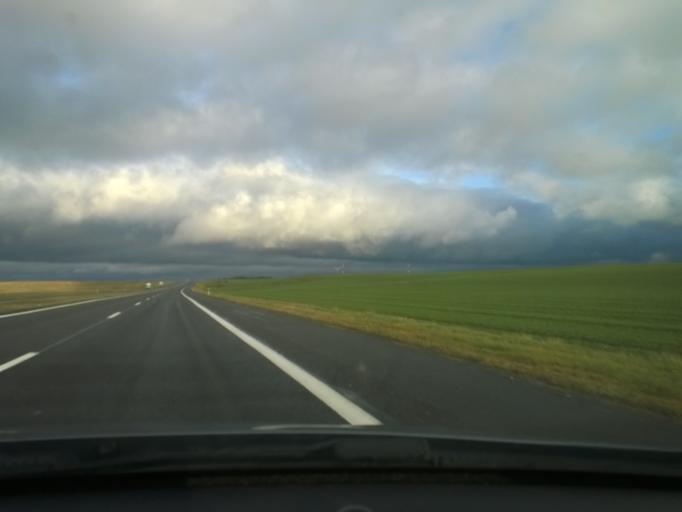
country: BY
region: Minsk
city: Snow
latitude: 53.2558
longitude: 26.2378
